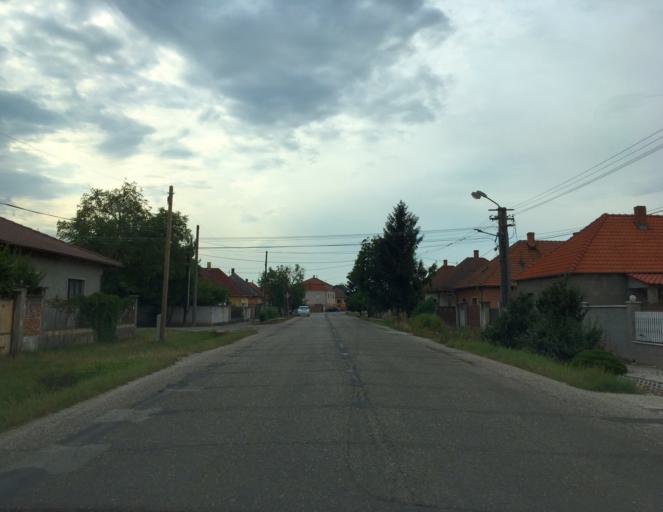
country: SK
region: Nitriansky
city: Kolarovo
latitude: 47.9114
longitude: 17.9909
